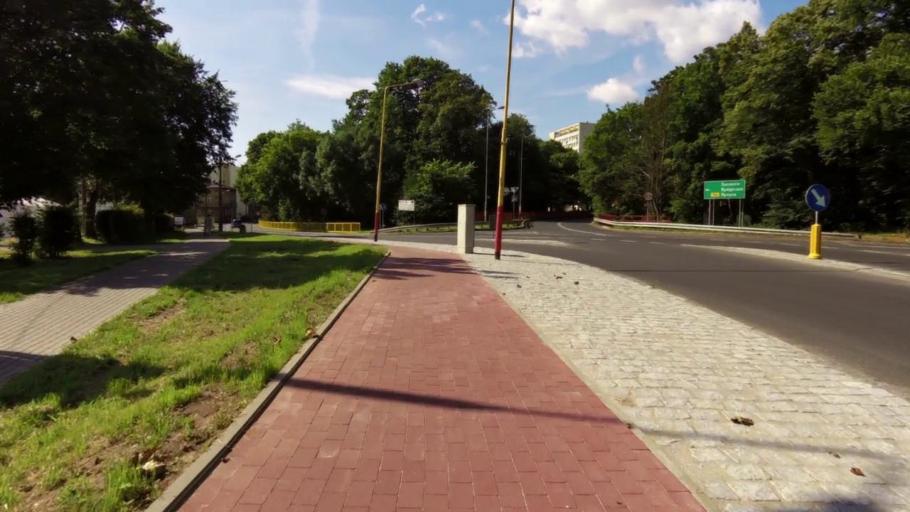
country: PL
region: West Pomeranian Voivodeship
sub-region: Powiat stargardzki
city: Stargard Szczecinski
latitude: 53.3422
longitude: 15.0507
